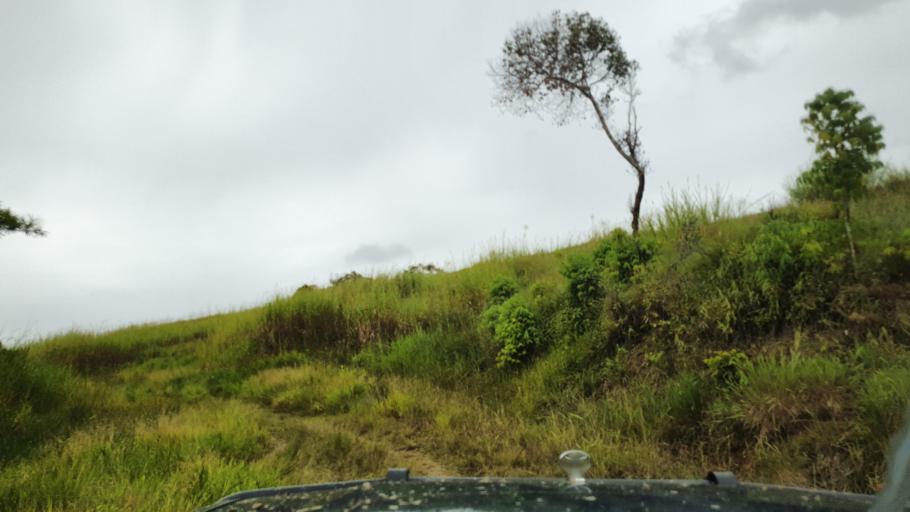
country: PG
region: Jiwaka
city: Minj
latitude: -5.9446
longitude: 144.7655
